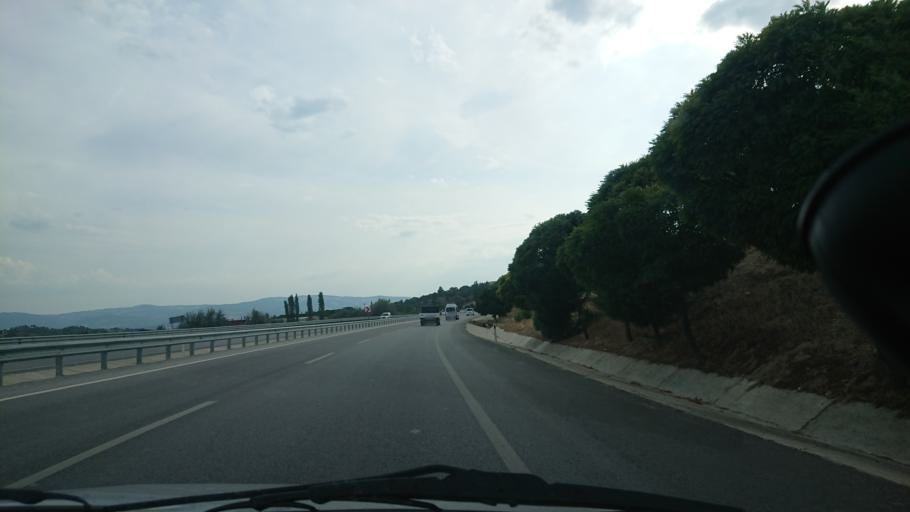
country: TR
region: Kuetahya
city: Gediz
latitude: 39.0177
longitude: 29.4124
